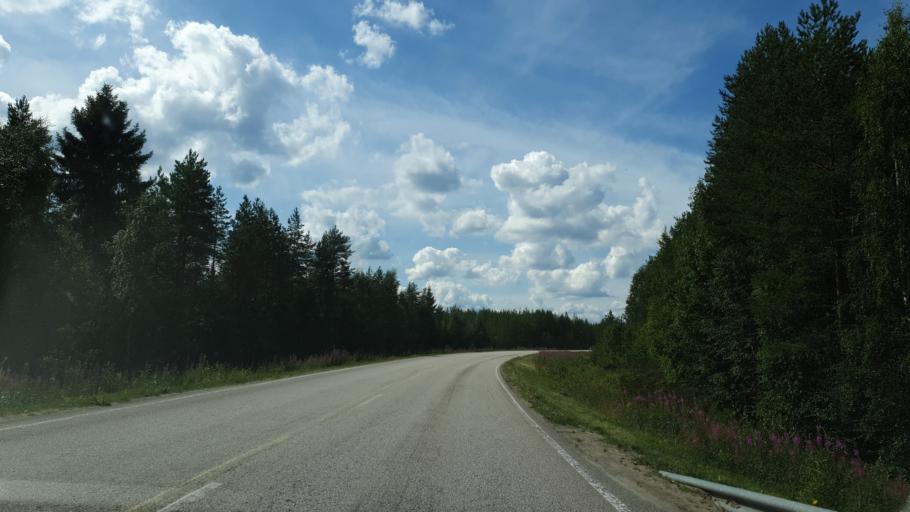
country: FI
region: Kainuu
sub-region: Kehys-Kainuu
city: Kuhmo
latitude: 64.1629
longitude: 29.3061
